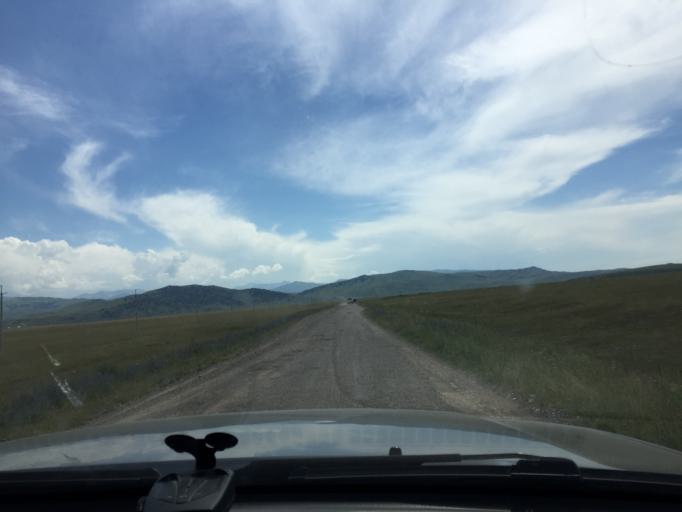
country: KZ
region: Almaty Oblysy
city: Kegen
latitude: 42.7982
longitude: 79.1781
